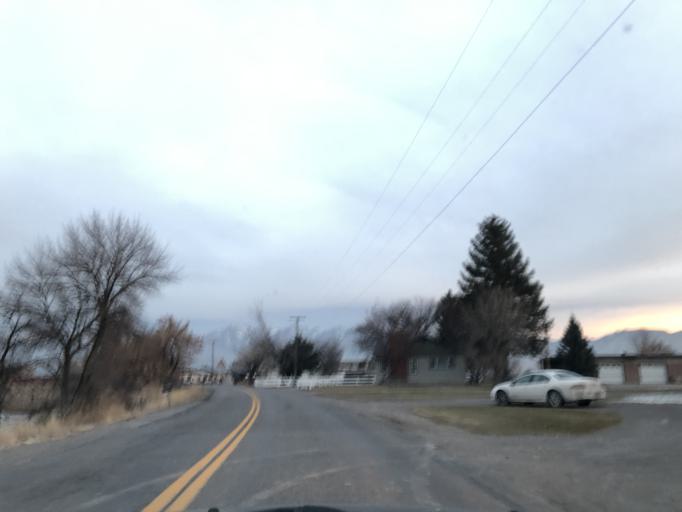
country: US
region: Utah
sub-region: Cache County
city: Benson
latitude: 41.7908
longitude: -111.9090
